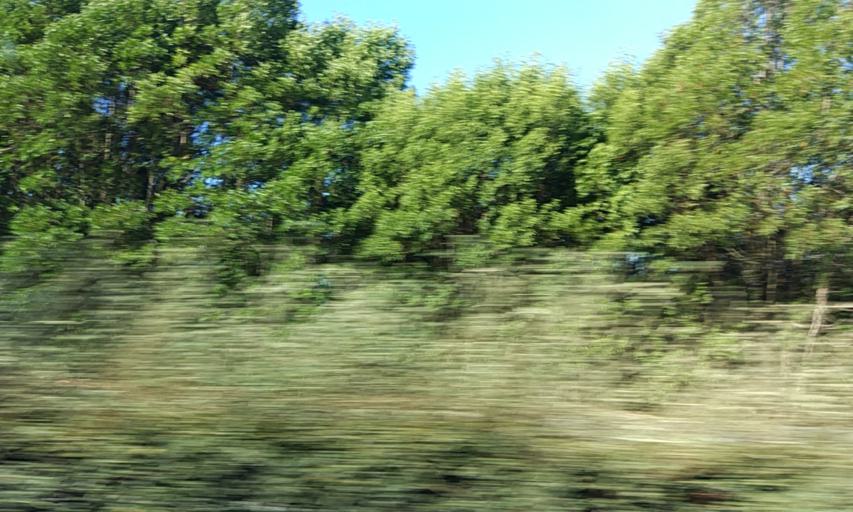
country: PT
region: Porto
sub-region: Paredes
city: Recarei
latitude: 41.1687
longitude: -8.4059
